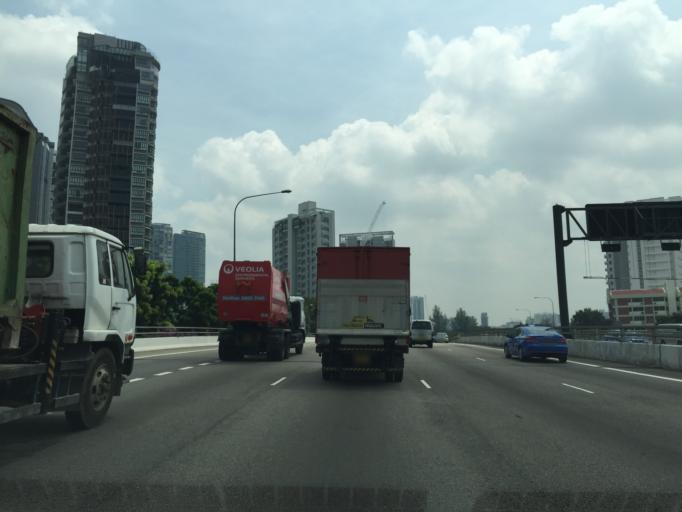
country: SG
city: Singapore
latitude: 1.3131
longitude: 103.8449
